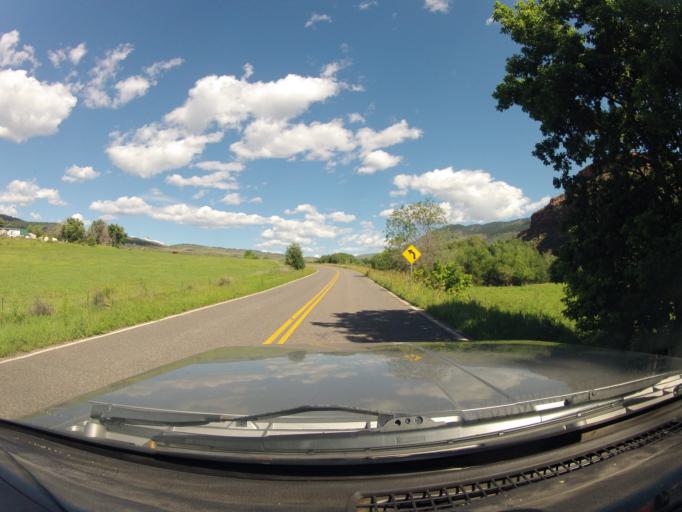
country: US
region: Colorado
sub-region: Larimer County
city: Laporte
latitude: 40.5079
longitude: -105.2415
